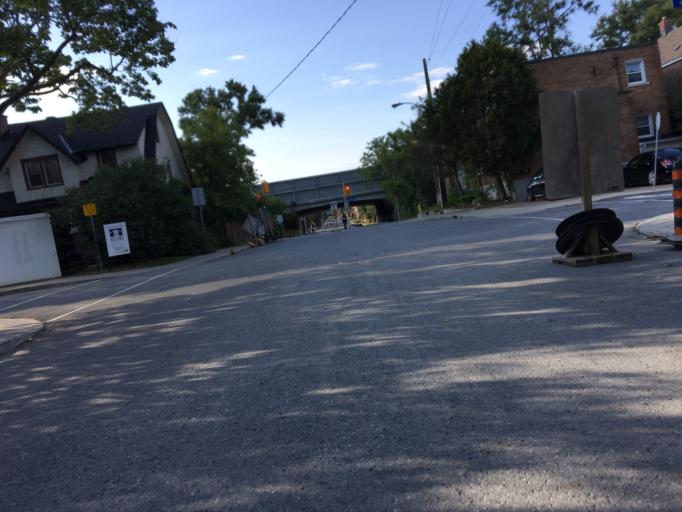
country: CA
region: Ontario
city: Ottawa
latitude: 45.4050
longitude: -75.6978
